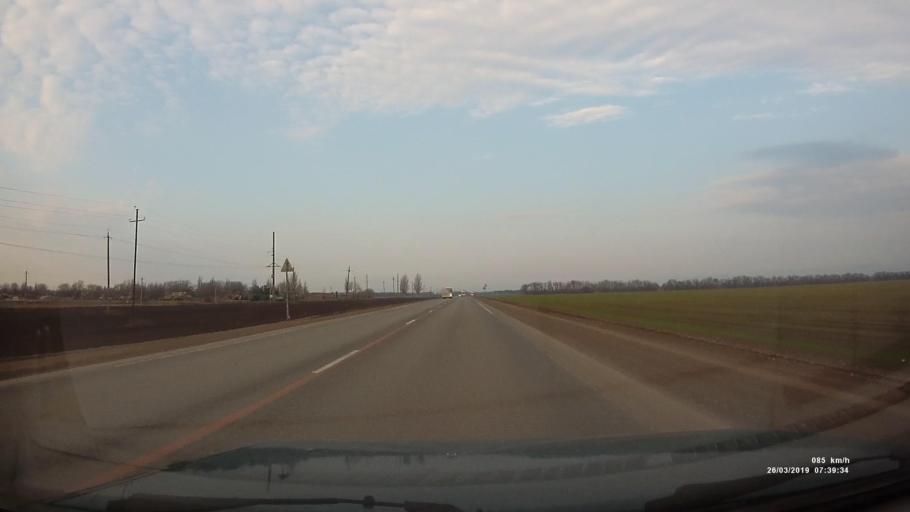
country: RU
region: Rostov
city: Novobessergenovka
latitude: 47.1969
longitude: 38.6631
